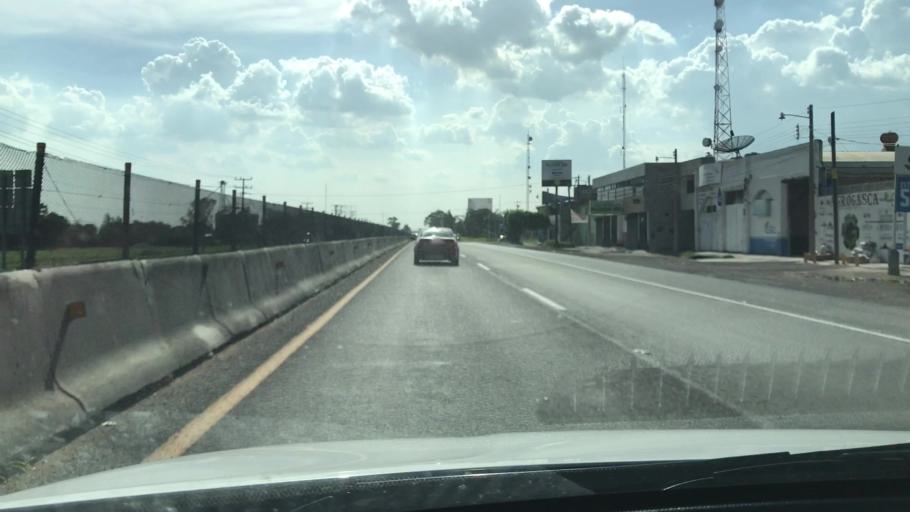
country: MX
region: Guanajuato
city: Villagran
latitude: 20.5091
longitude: -100.9997
